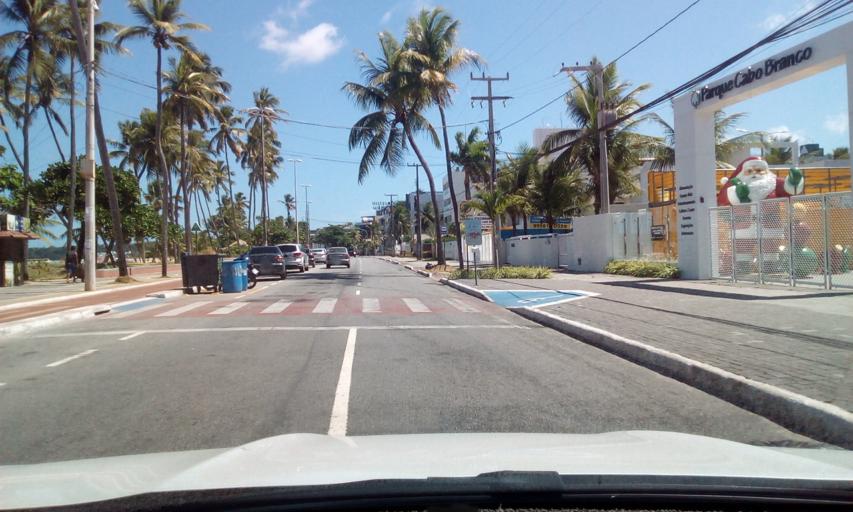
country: BR
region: Paraiba
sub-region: Joao Pessoa
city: Joao Pessoa
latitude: -7.1315
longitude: -34.8219
